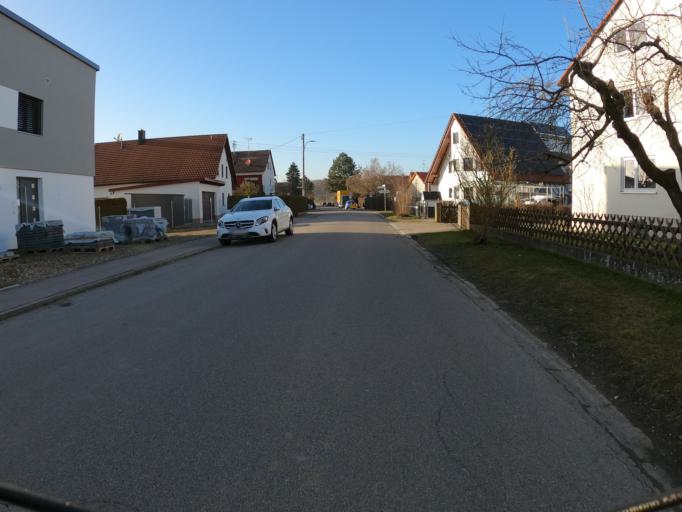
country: DE
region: Bavaria
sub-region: Swabia
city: Holzheim
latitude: 48.4014
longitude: 10.1052
